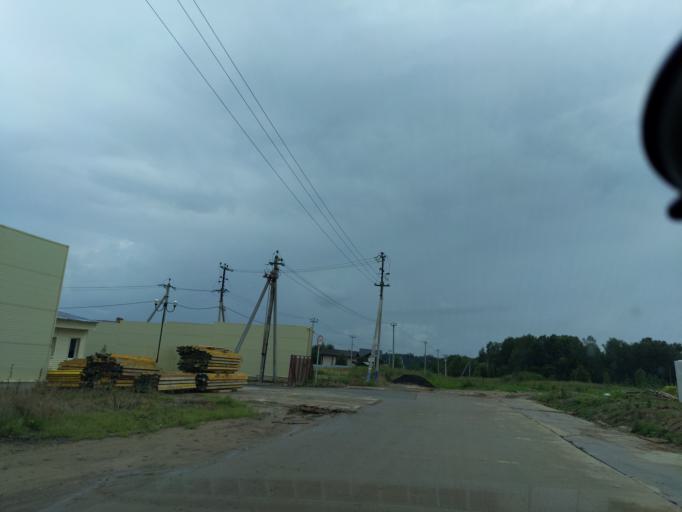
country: RU
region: Moskovskaya
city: Lugovaya
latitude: 56.0602
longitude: 37.5018
